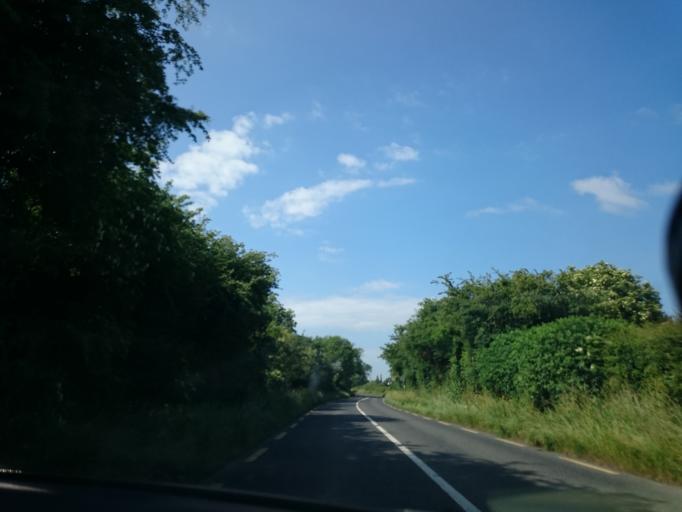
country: IE
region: Leinster
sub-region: Kilkenny
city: Thomastown
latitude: 52.5514
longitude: -7.2275
